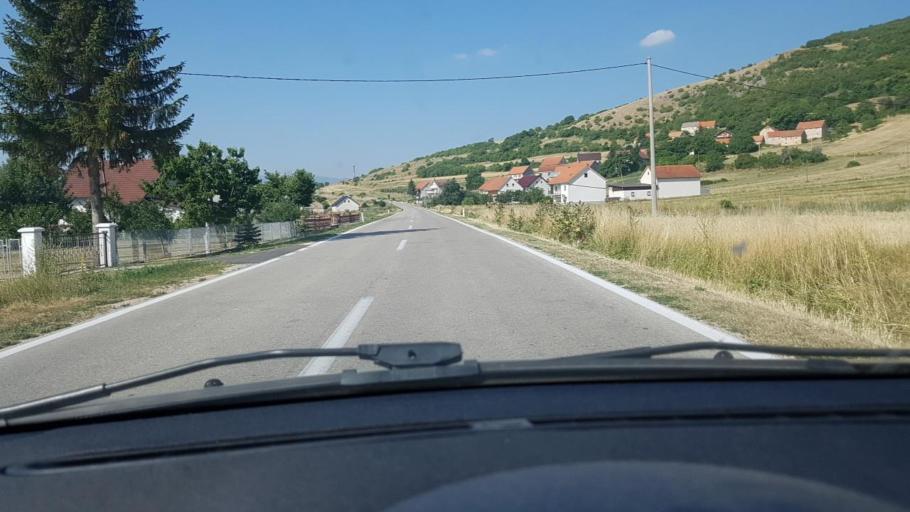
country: BA
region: Federation of Bosnia and Herzegovina
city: Zabrisce
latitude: 43.8683
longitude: 16.9112
